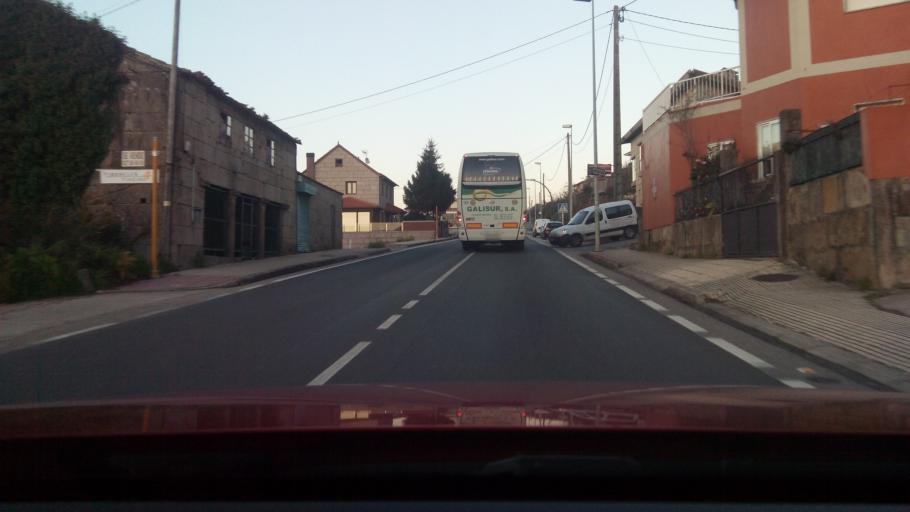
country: ES
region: Galicia
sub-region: Provincia de Pontevedra
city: Gondomar
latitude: 42.1454
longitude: -8.7288
